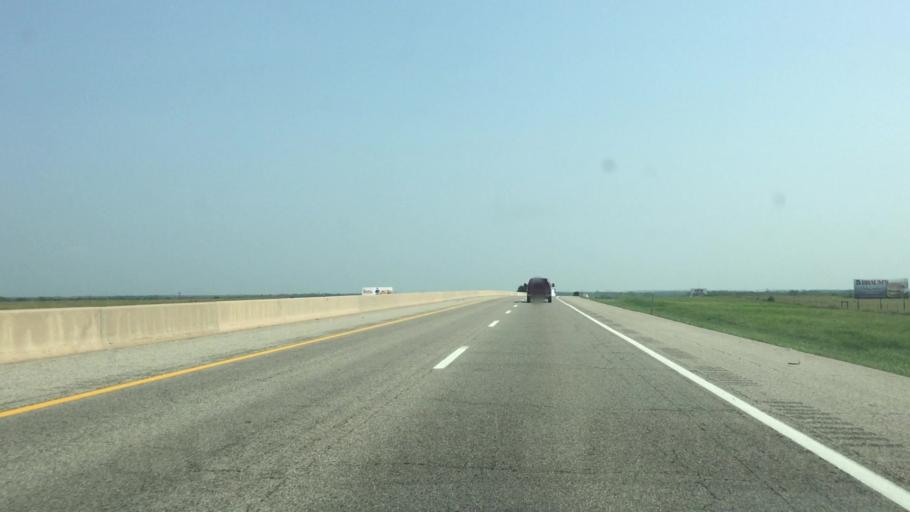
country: US
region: Kansas
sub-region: Lyon County
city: Emporia
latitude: 38.3497
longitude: -96.2894
